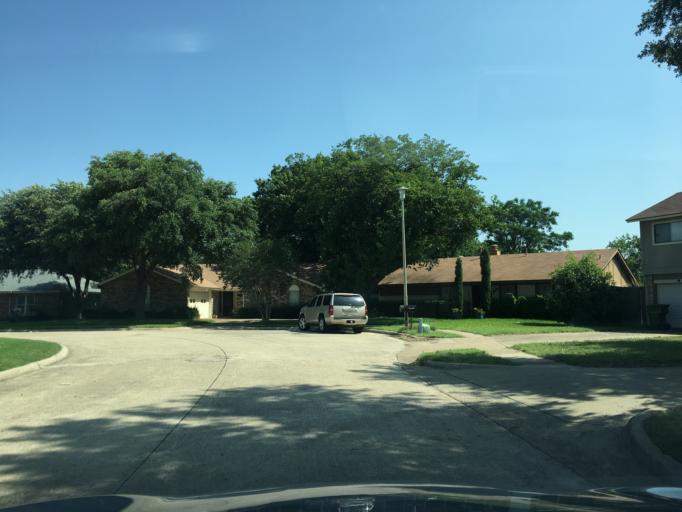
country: US
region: Texas
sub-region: Dallas County
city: Richardson
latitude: 32.9287
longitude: -96.6858
